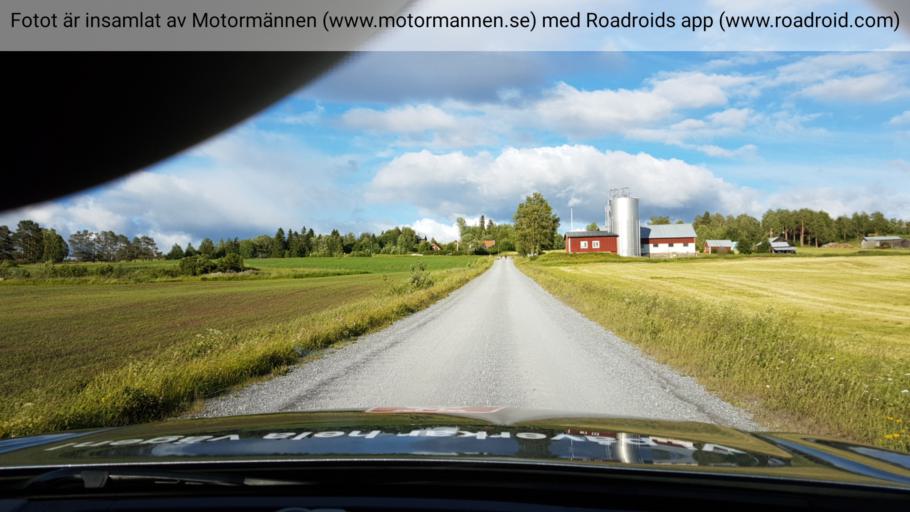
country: SE
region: Jaemtland
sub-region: Bergs Kommun
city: Hoverberg
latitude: 62.9979
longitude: 14.3819
